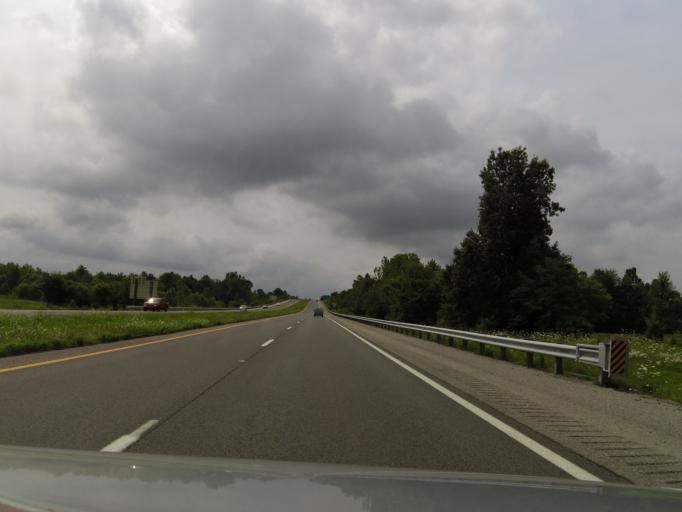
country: US
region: Kentucky
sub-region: Hopkins County
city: Madisonville
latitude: 37.3462
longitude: -87.4829
